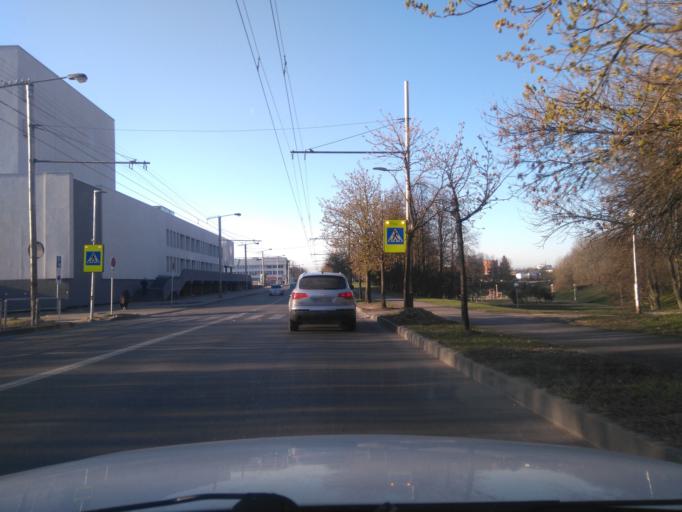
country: LT
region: Kauno apskritis
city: Dainava (Kaunas)
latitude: 54.9077
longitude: 23.9738
